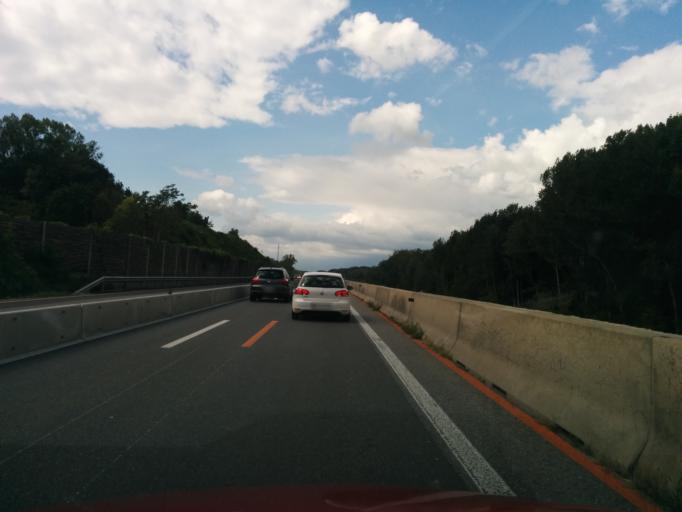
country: AT
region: Lower Austria
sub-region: Politischer Bezirk Wien-Umgebung
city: Fischamend Dorf
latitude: 48.1246
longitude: 16.6012
